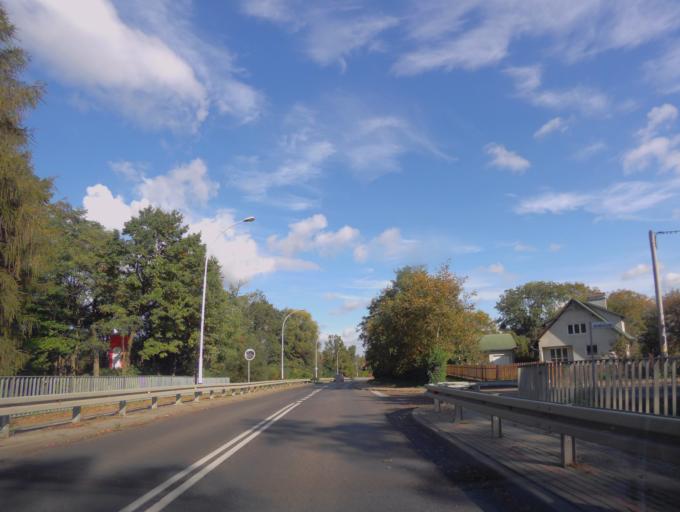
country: PL
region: Subcarpathian Voivodeship
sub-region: Powiat lezajski
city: Lezajsk
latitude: 50.2466
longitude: 22.4136
